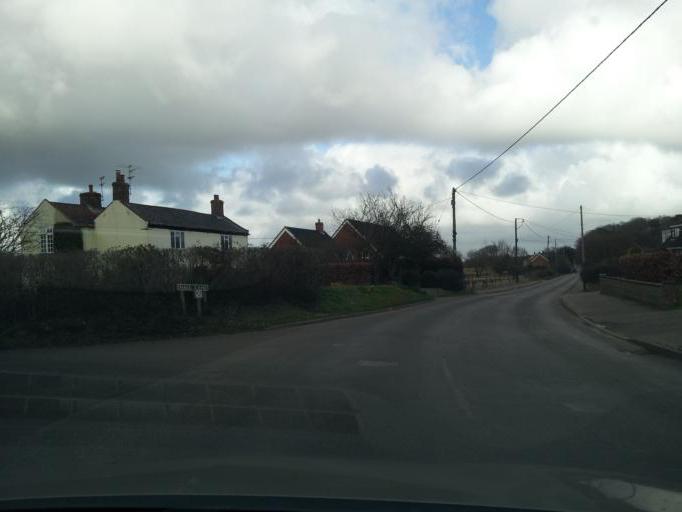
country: GB
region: England
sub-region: Norfolk
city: Horsford
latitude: 52.7185
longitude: 1.2113
